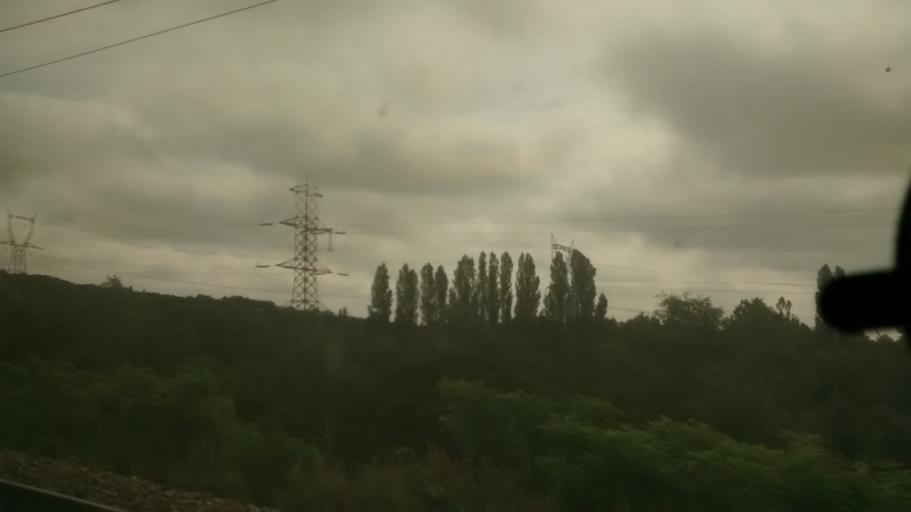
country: FR
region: Ile-de-France
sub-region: Departement de l'Essonne
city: Briis-sous-Forges
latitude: 48.6209
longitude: 2.1342
